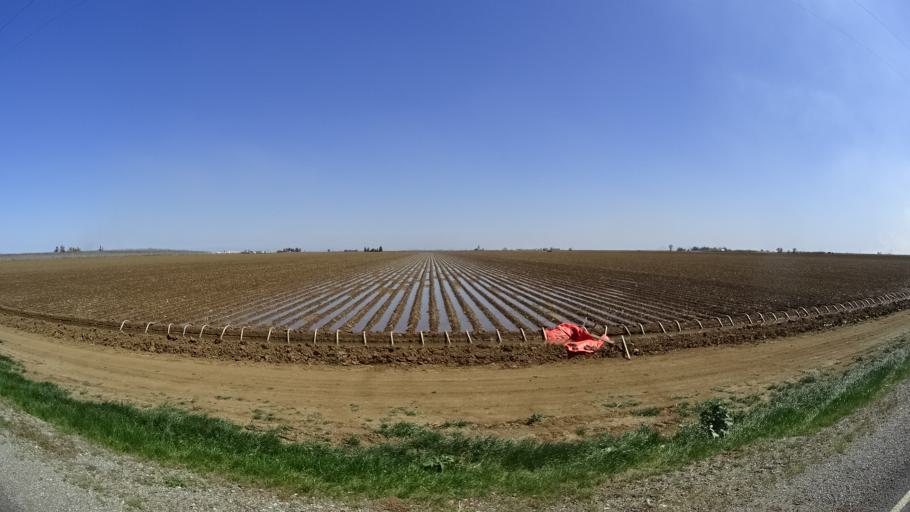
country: US
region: California
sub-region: Glenn County
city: Willows
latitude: 39.4433
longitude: -122.2487
